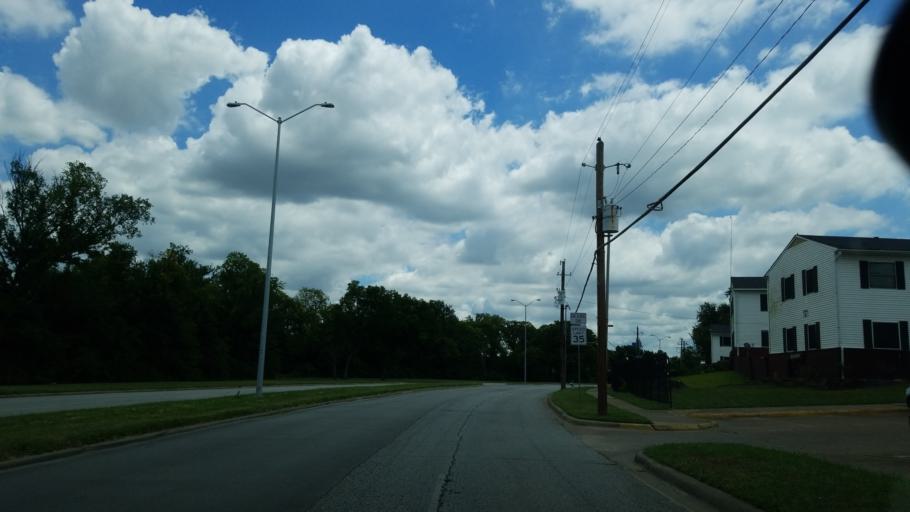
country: US
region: Texas
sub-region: Dallas County
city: Dallas
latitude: 32.7212
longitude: -96.7714
